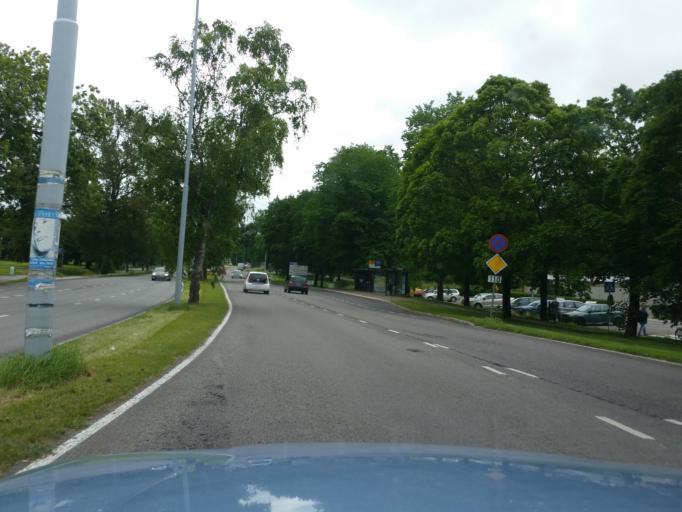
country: FI
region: Varsinais-Suomi
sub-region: Turku
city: Turku
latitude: 60.4368
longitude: 22.2921
